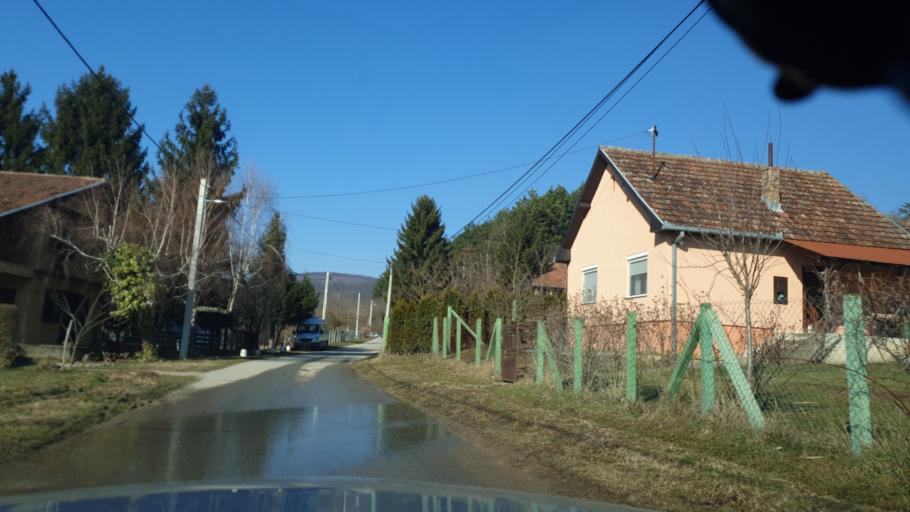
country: RS
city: Vrdnik
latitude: 45.1131
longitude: 19.7672
